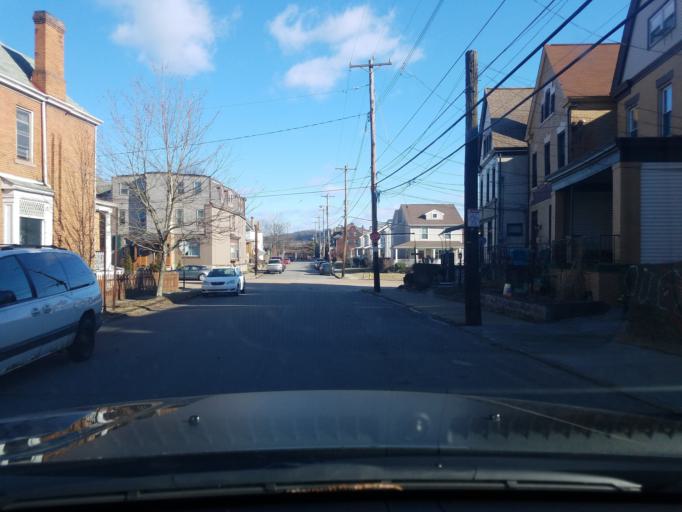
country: US
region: Pennsylvania
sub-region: Allegheny County
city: Wilkinsburg
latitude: 40.4442
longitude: -79.8935
